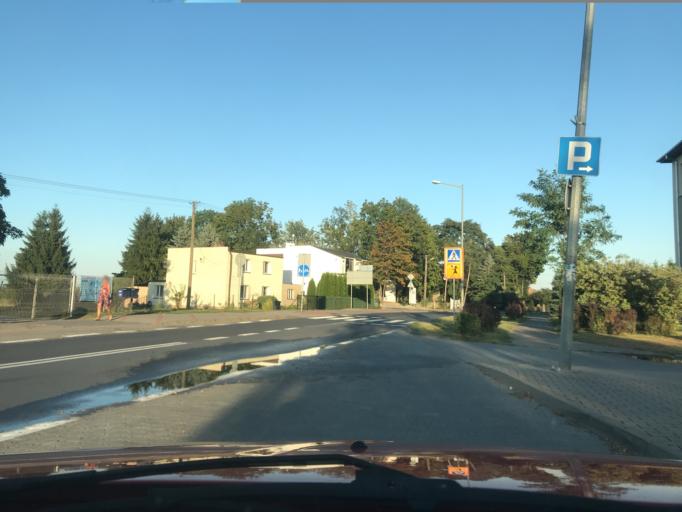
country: PL
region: Greater Poland Voivodeship
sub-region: Powiat poznanski
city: Tarnowo Podgorne
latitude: 52.4334
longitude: 16.7018
